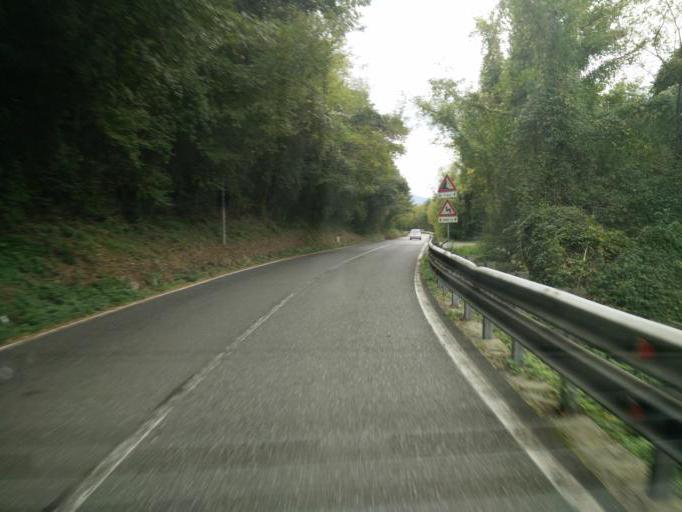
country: IT
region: Tuscany
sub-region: Provincia di Massa-Carrara
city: Fivizzano
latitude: 44.2199
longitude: 10.0982
